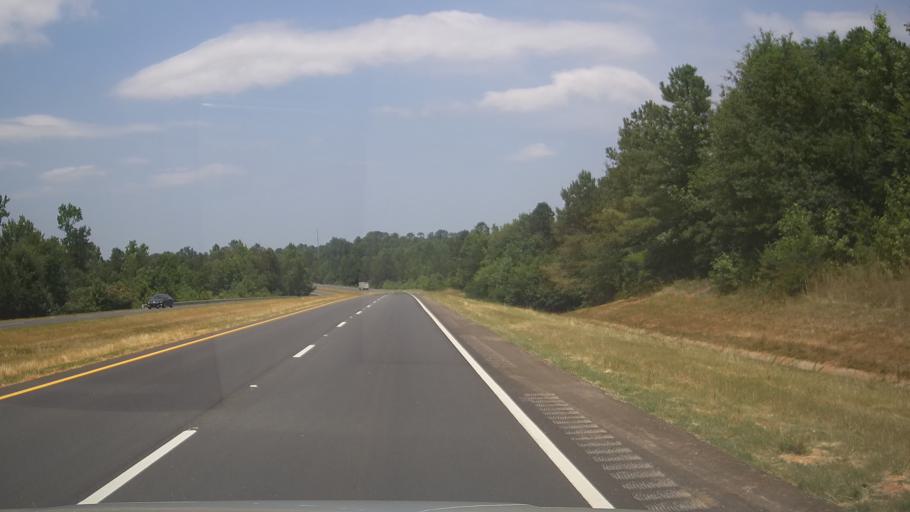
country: US
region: Georgia
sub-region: Jackson County
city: Commerce
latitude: 34.1972
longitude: -83.4321
